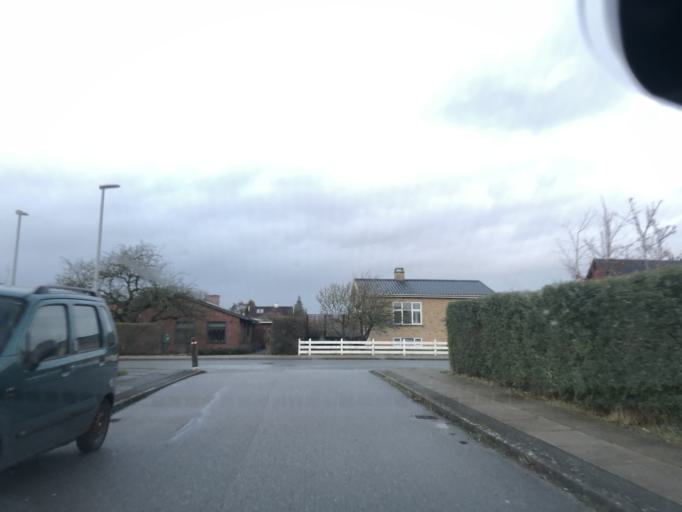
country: DK
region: Capital Region
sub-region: Tarnby Kommune
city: Tarnby
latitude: 55.6135
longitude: 12.6036
